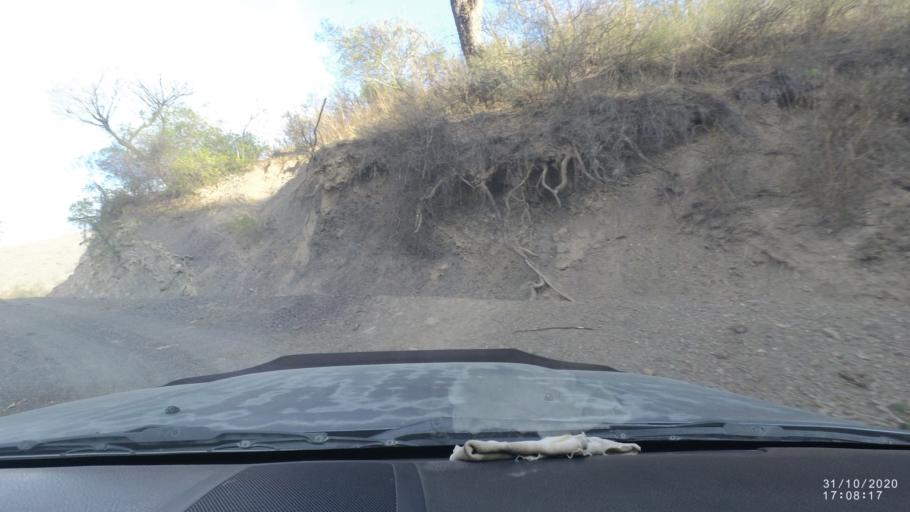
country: BO
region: Chuquisaca
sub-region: Provincia Zudanez
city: Mojocoya
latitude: -18.5463
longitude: -64.5405
